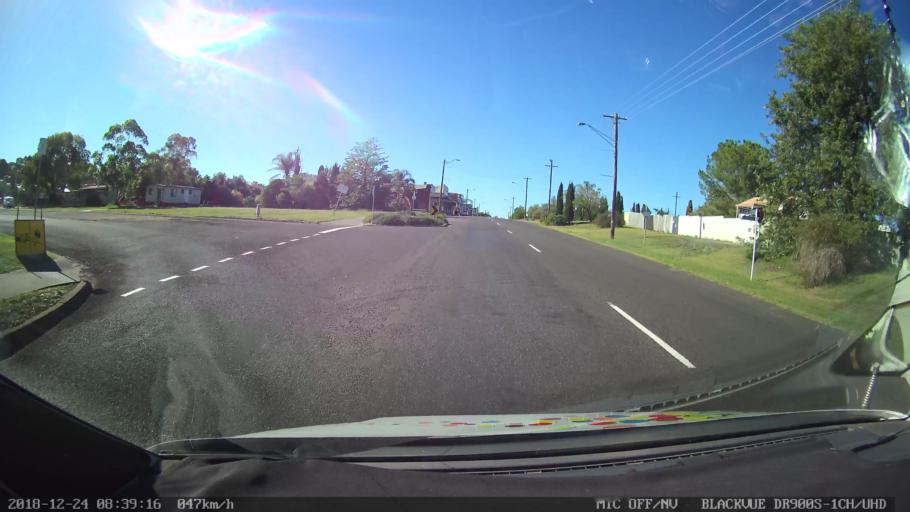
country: AU
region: New South Wales
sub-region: Liverpool Plains
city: Quirindi
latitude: -31.3468
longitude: 150.6473
